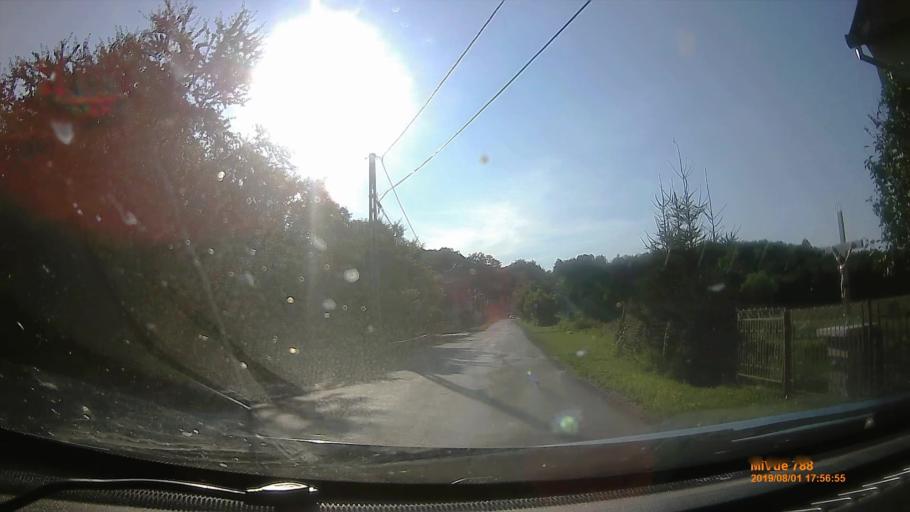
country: HU
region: Baranya
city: Sasd
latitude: 46.1984
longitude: 18.1182
